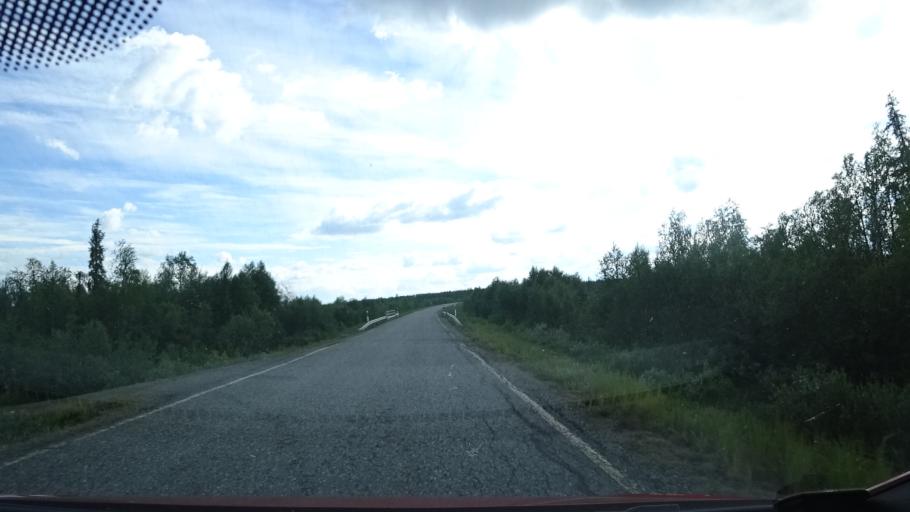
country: FI
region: Lapland
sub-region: Tunturi-Lappi
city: Kittilae
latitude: 68.2499
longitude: 25.8458
